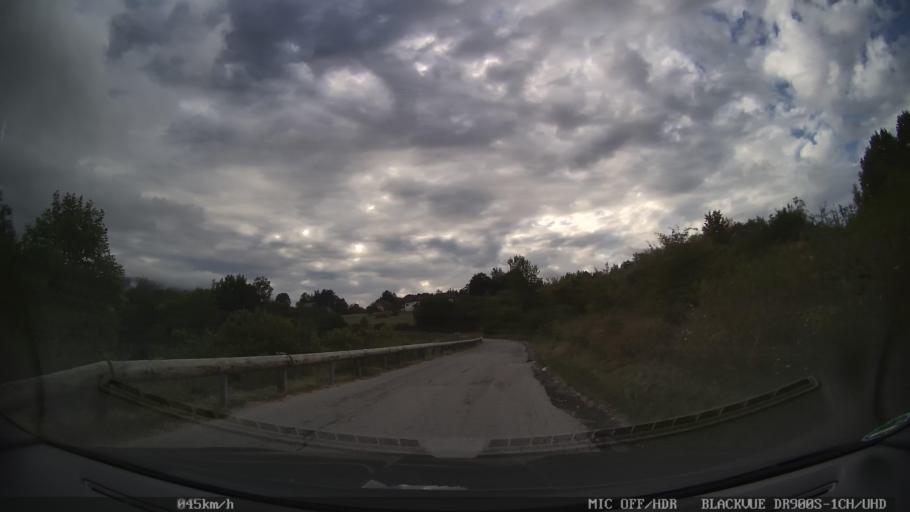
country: HR
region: Licko-Senjska
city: Jezerce
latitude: 44.9244
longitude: 15.5999
